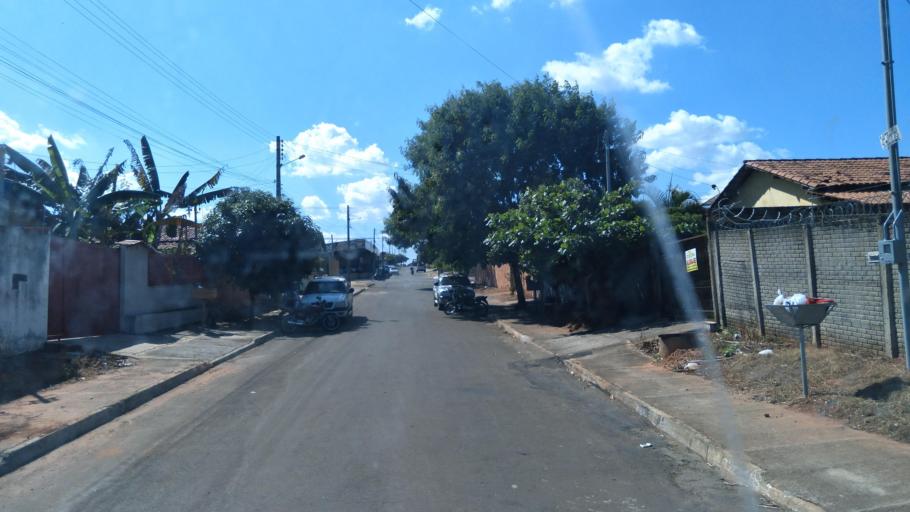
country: BR
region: Goias
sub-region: Mineiros
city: Mineiros
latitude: -17.5491
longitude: -52.5421
